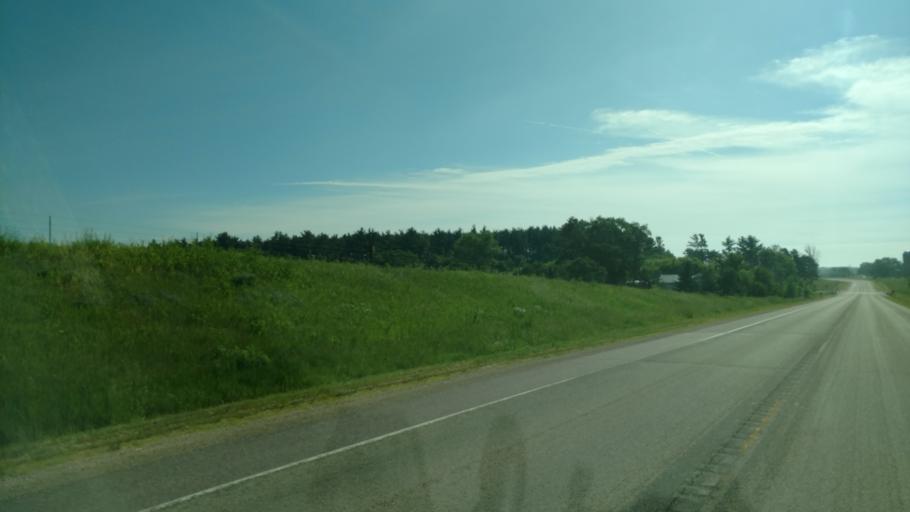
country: US
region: Wisconsin
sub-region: Sauk County
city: Lake Delton
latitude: 43.5474
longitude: -89.8534
